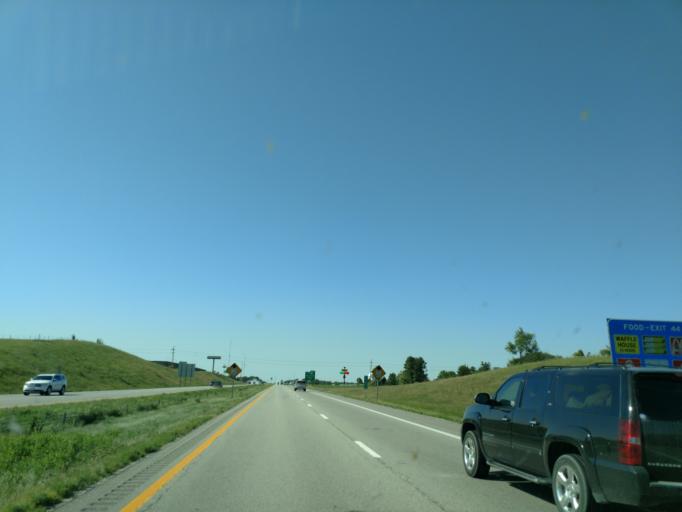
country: US
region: Missouri
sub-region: Buchanan County
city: Saint Joseph
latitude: 39.7162
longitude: -94.7885
